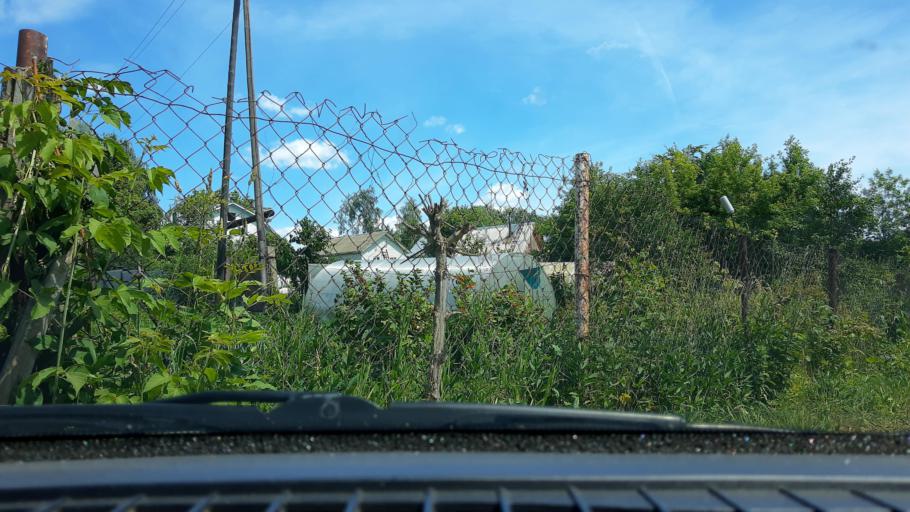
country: RU
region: Nizjnij Novgorod
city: Burevestnik
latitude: 56.1873
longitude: 43.9283
